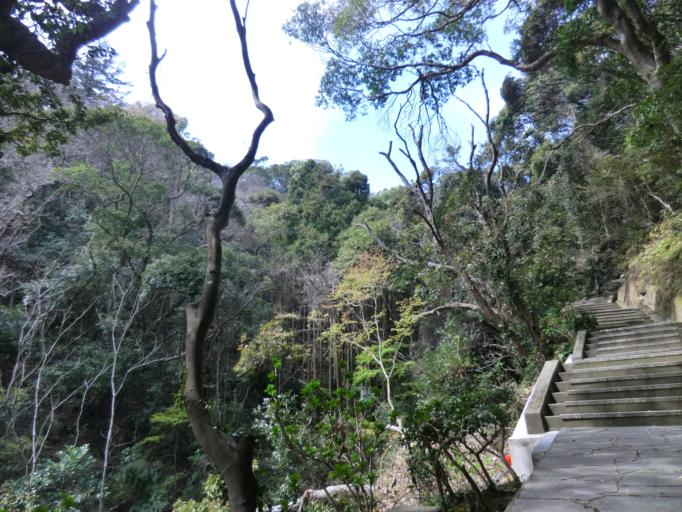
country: JP
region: Chiba
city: Futtsu
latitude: 35.1542
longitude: 139.8325
